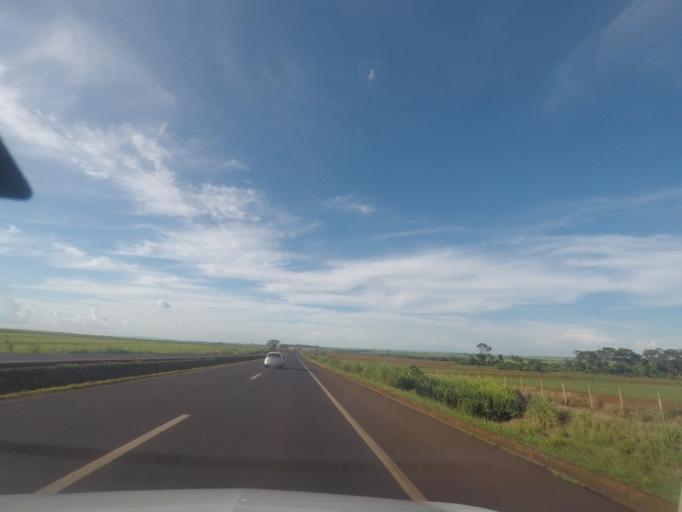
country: BR
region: Minas Gerais
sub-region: Centralina
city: Centralina
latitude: -18.5627
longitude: -49.1937
